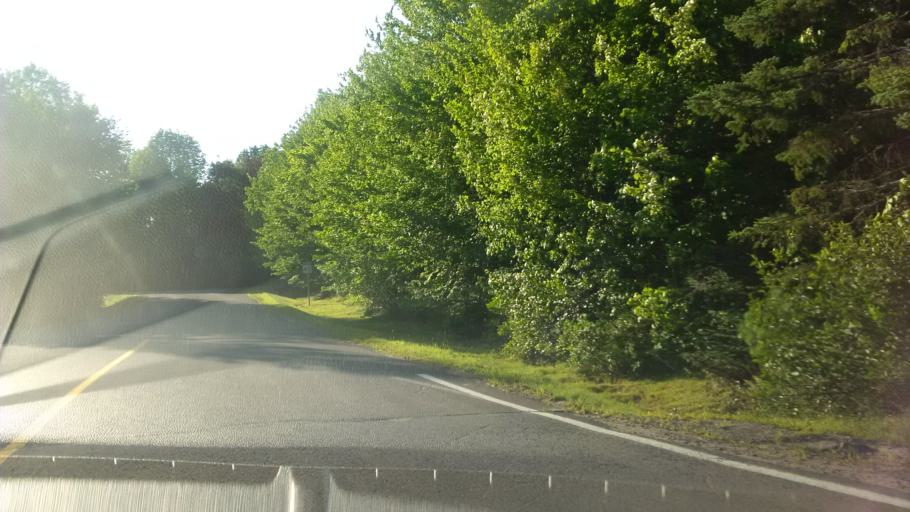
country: CA
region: New Brunswick
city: Fredericton
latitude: 45.8881
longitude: -66.6868
